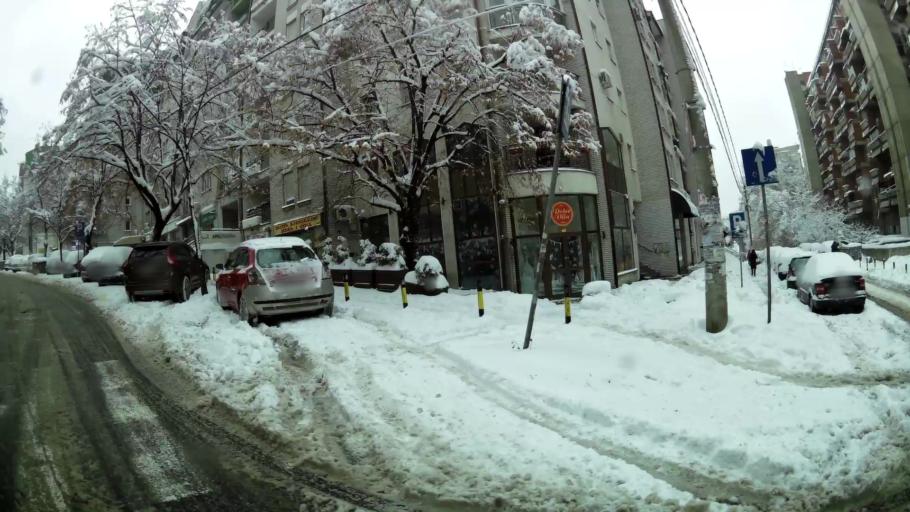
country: RS
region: Central Serbia
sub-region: Belgrade
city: Vracar
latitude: 44.7927
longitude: 20.4783
